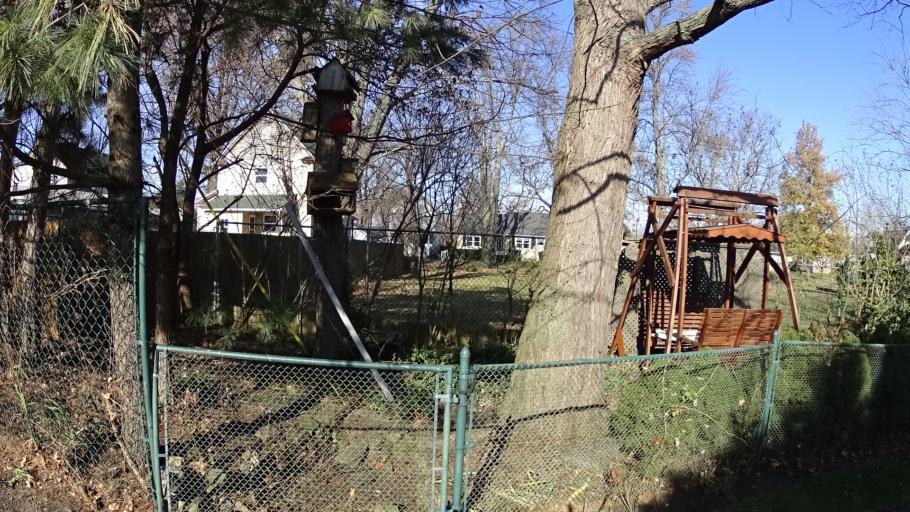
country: US
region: Ohio
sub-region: Lorain County
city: Elyria
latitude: 41.3817
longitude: -82.1146
